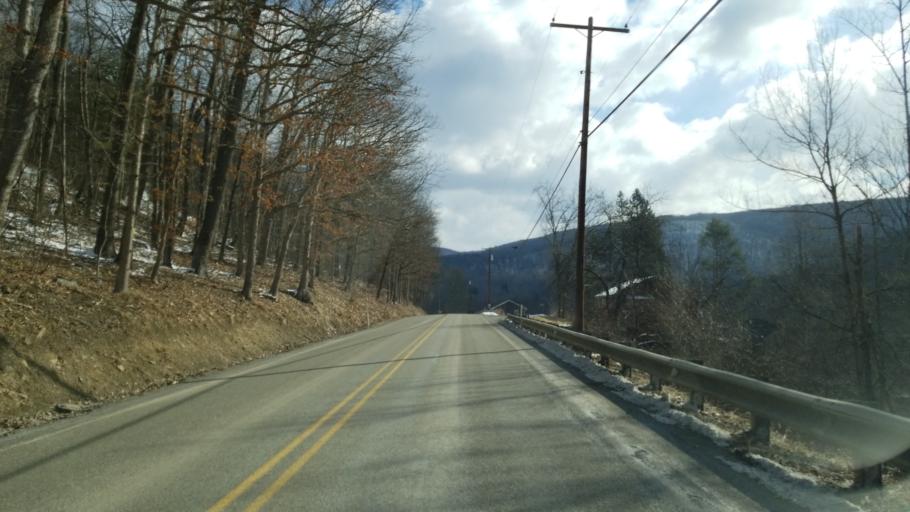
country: US
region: Pennsylvania
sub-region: Elk County
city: Saint Marys
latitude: 41.2847
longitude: -78.4050
